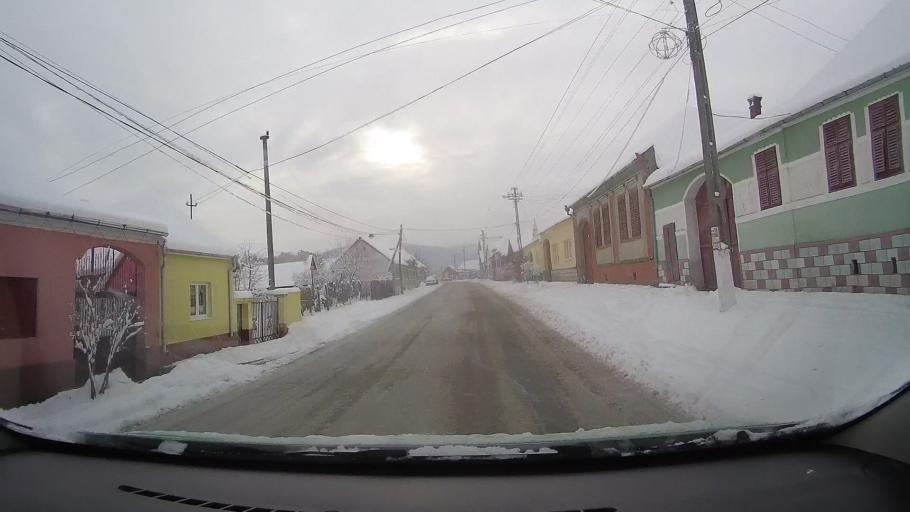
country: RO
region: Alba
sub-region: Comuna Pianu
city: Pianu de Jos
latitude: 45.9365
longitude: 23.4857
